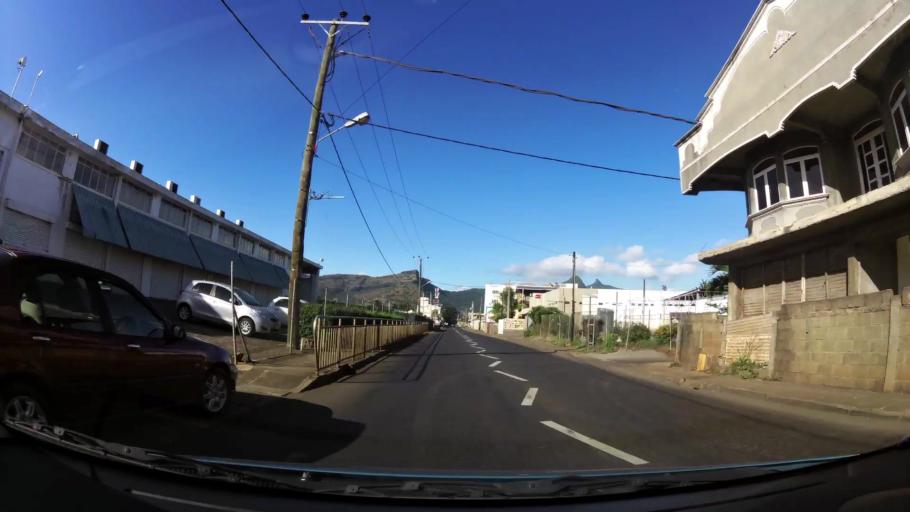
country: MU
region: Black River
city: Petite Riviere
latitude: -20.1834
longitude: 57.4660
